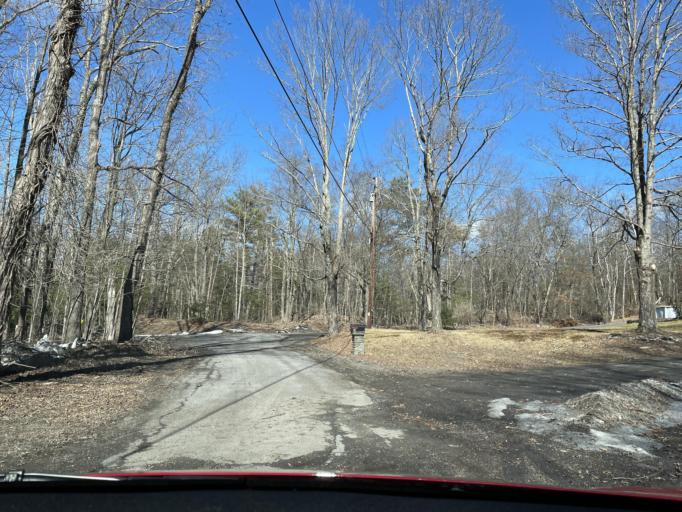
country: US
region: New York
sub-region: Ulster County
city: West Hurley
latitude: 41.9762
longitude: -74.0790
